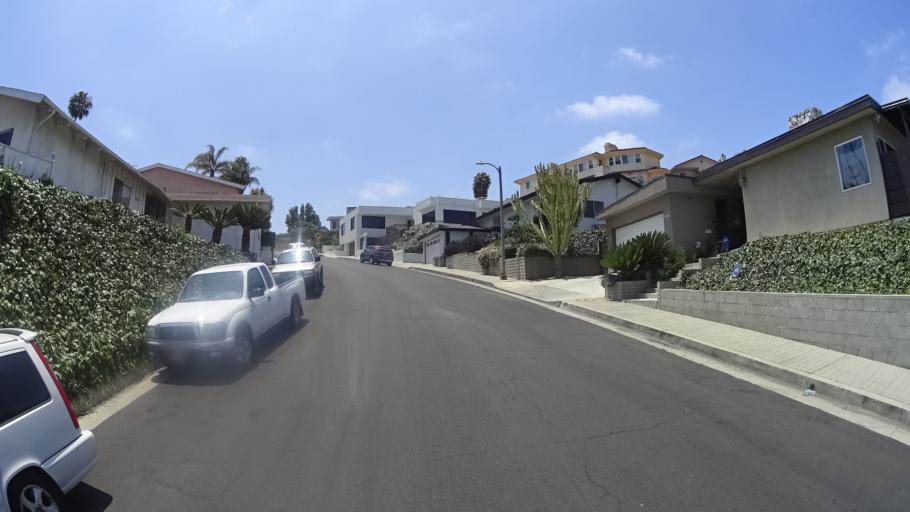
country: US
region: California
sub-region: Los Angeles County
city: View Park-Windsor Hills
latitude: 34.0101
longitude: -118.3553
